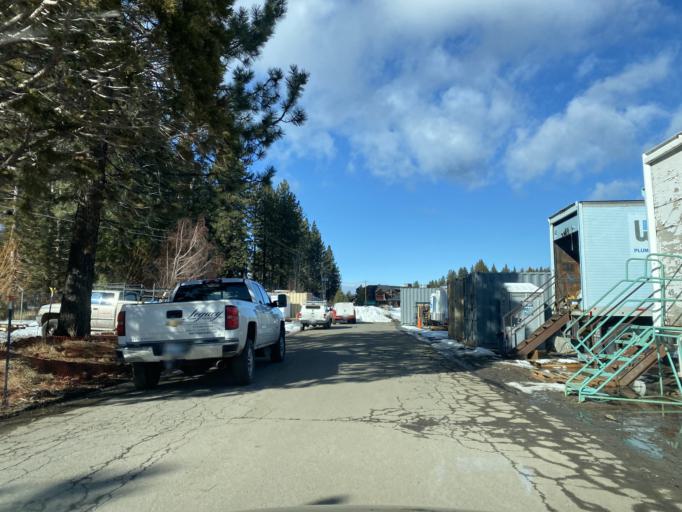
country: US
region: Nevada
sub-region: Douglas County
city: Kingsbury
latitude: 38.9736
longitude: -119.9448
